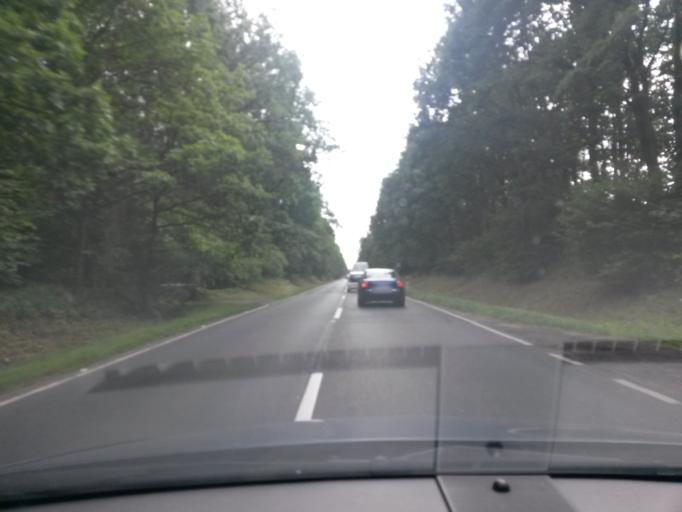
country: PL
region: Greater Poland Voivodeship
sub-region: Powiat poznanski
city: Kornik
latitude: 52.1988
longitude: 17.0631
